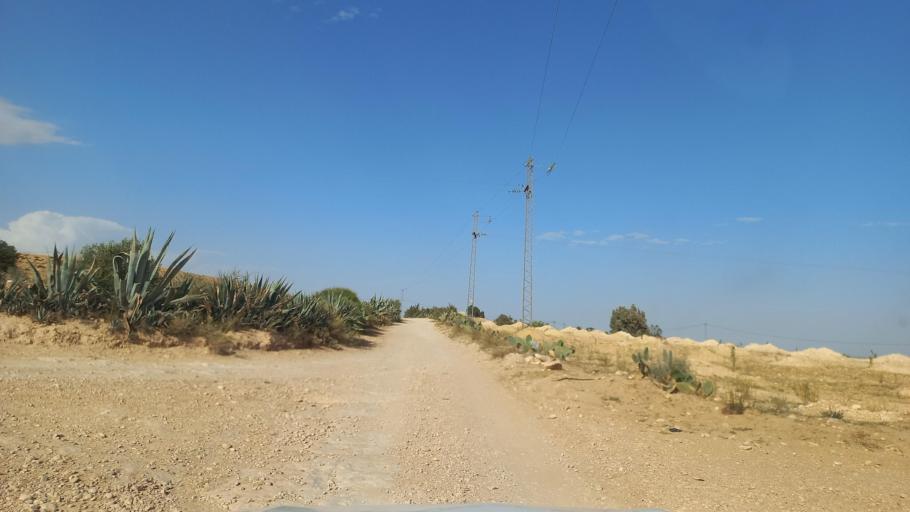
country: TN
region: Al Qasrayn
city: Kasserine
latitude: 35.2539
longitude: 8.9320
